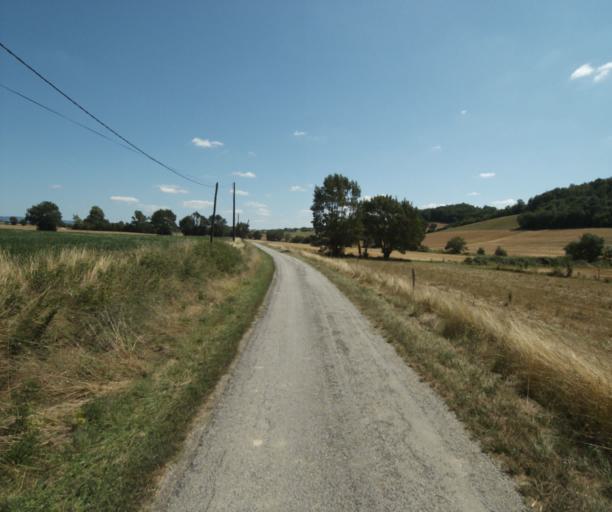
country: FR
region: Midi-Pyrenees
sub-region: Departement de la Haute-Garonne
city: Auriac-sur-Vendinelle
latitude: 43.5006
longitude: 1.8618
